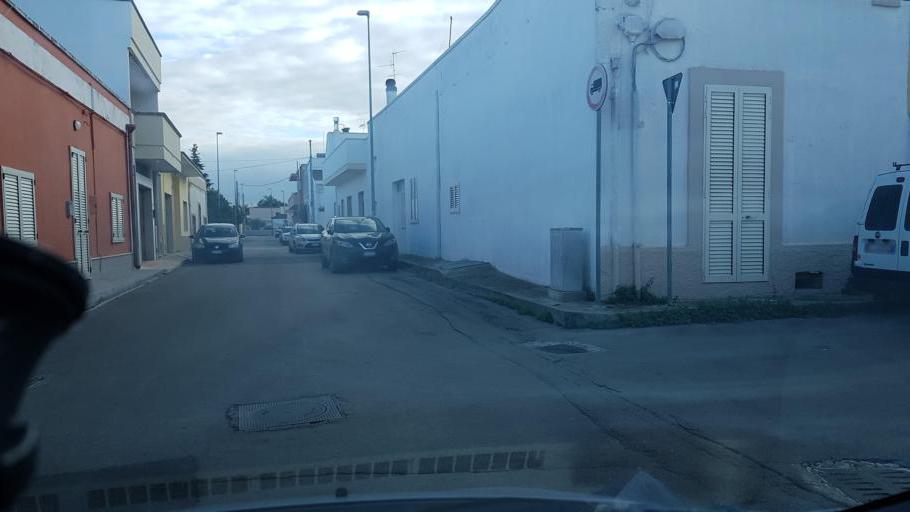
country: IT
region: Apulia
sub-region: Provincia di Lecce
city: Veglie
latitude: 40.3409
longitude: 17.9711
